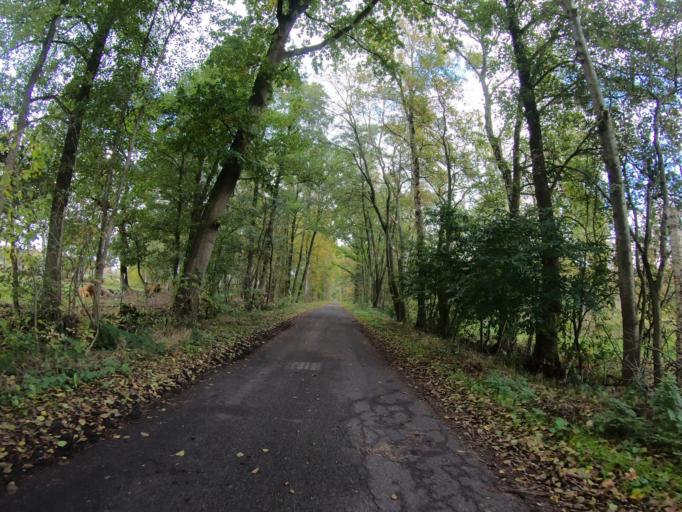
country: DE
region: Lower Saxony
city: Wagenhoff
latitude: 52.5487
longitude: 10.5552
